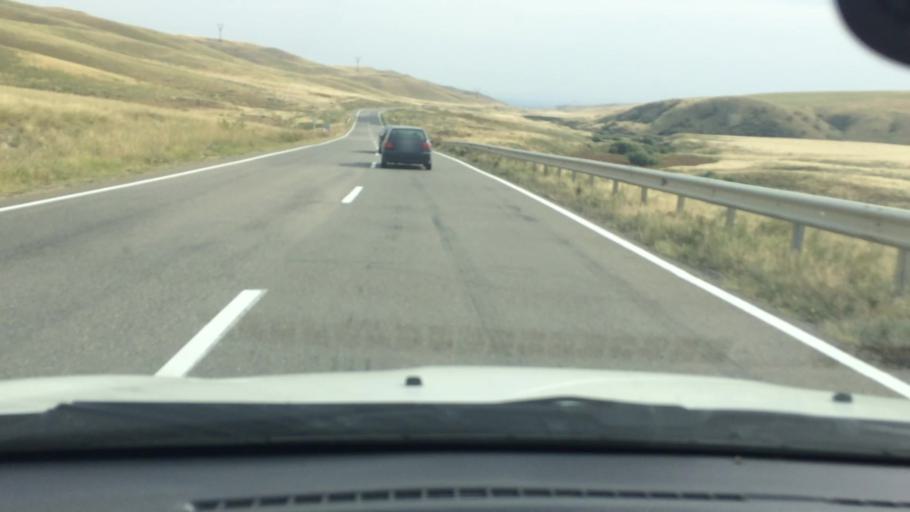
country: GE
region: Kvemo Kartli
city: Rust'avi
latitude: 41.5216
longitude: 44.9382
